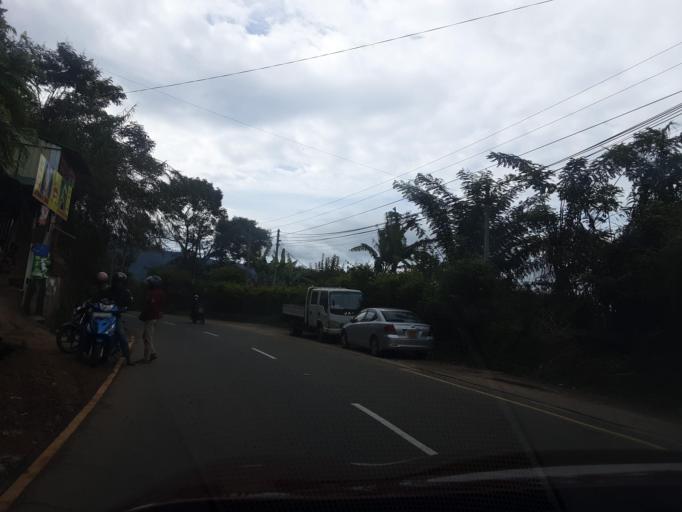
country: LK
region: Uva
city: Haputale
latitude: 6.8425
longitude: 80.9738
